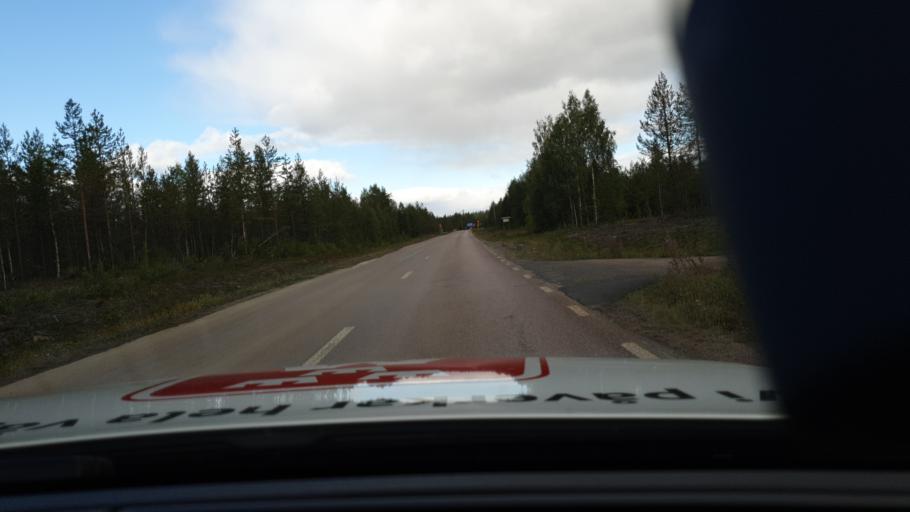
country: SE
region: Norrbotten
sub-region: Pajala Kommun
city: Pajala
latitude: 67.2506
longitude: 22.7811
